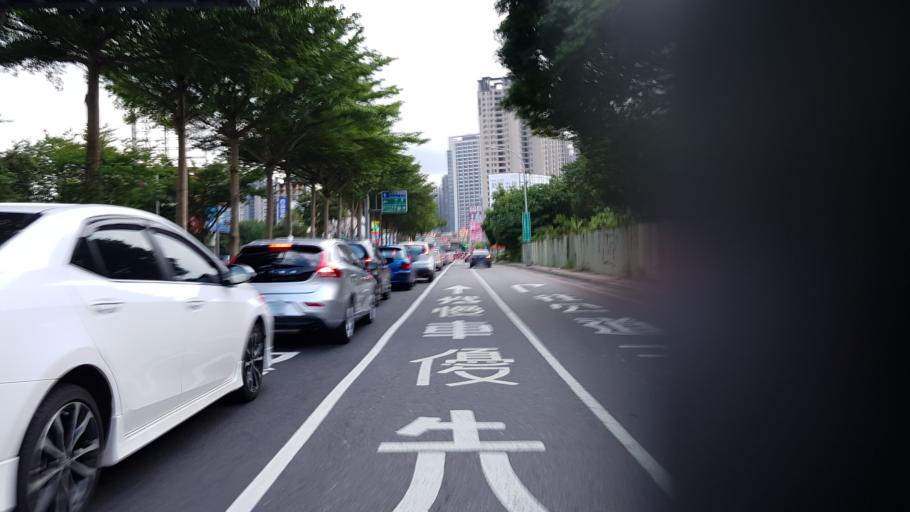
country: TW
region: Taiwan
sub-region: Hsinchu
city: Zhubei
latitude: 24.7978
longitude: 121.0133
